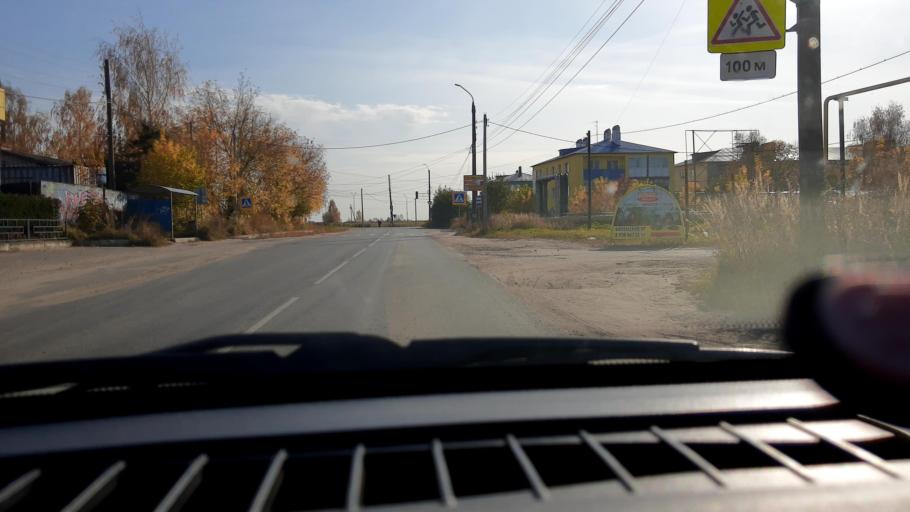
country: RU
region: Nizjnij Novgorod
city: Gorodets
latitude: 56.6414
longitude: 43.4896
